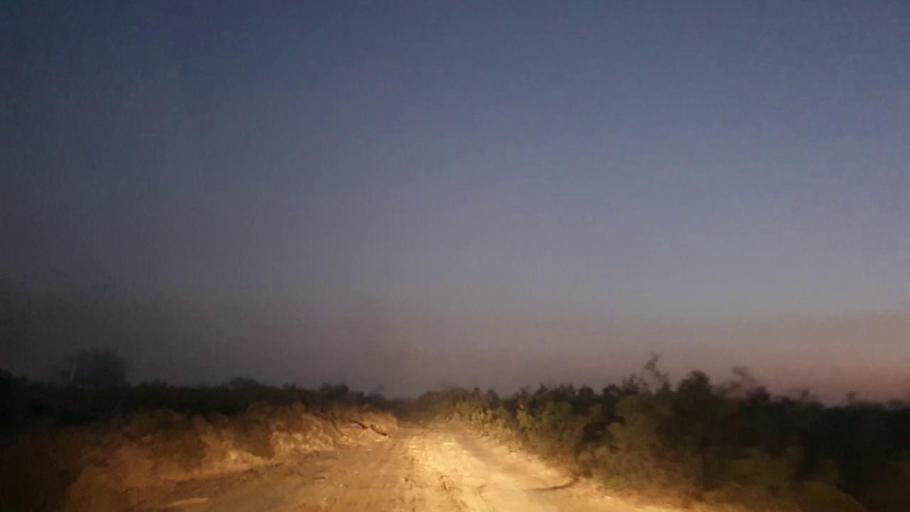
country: PK
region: Sindh
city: Nawabshah
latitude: 26.3213
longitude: 68.3791
